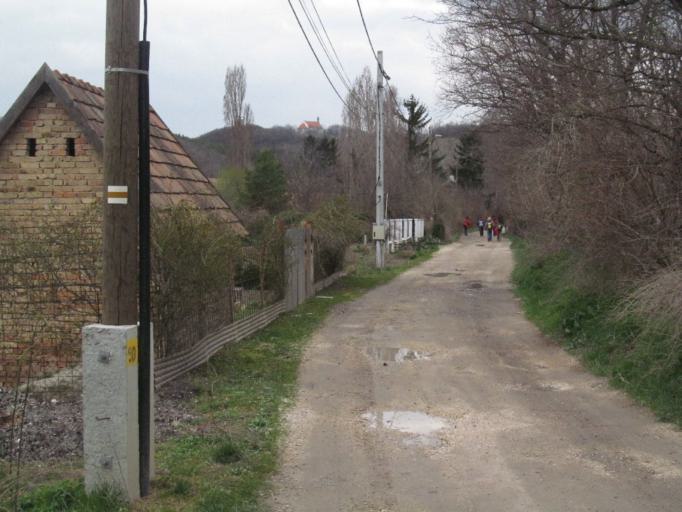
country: HU
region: Gyor-Moson-Sopron
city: Pannonhalma
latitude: 47.5430
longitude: 17.7738
